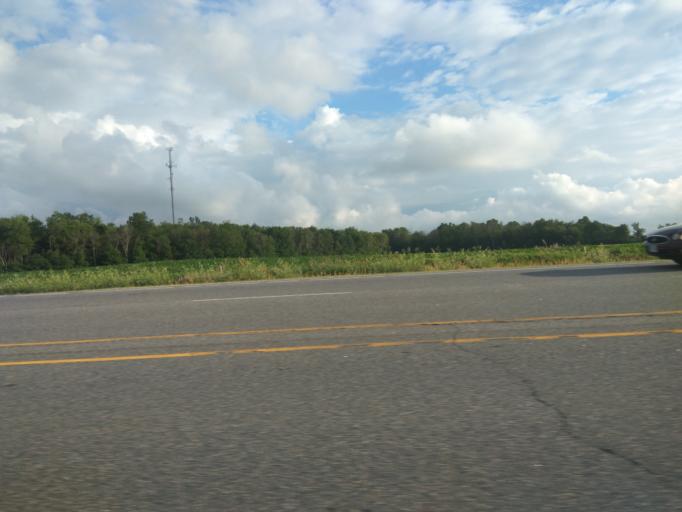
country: CA
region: Ontario
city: Kitchener
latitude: 43.3633
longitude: -80.7216
